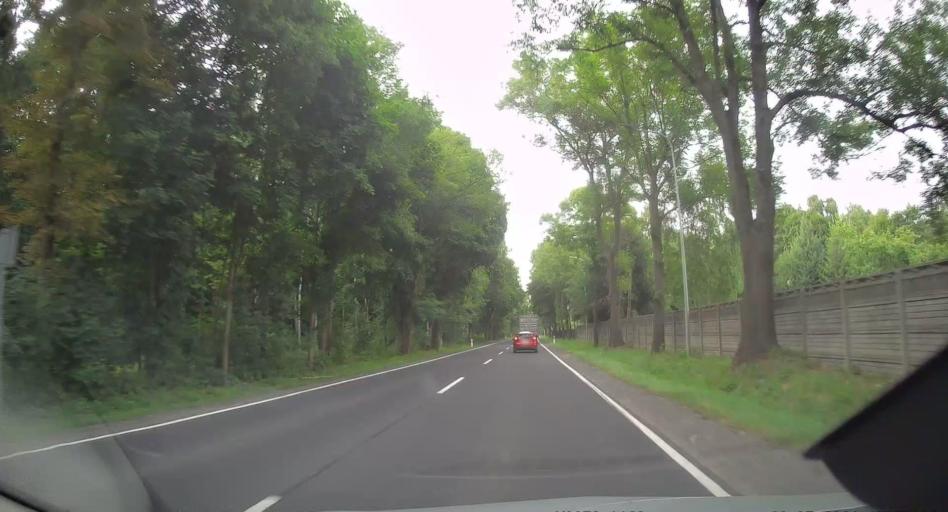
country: PL
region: Lodz Voivodeship
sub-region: Powiat radomszczanski
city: Gomunice
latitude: 51.1699
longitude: 19.4935
